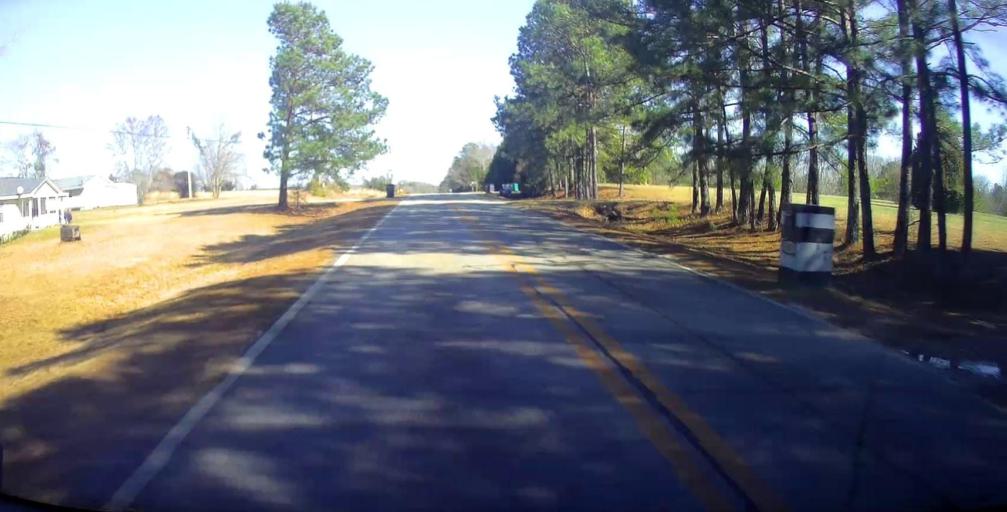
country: US
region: Georgia
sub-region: Peach County
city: Byron
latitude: 32.6111
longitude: -83.8195
